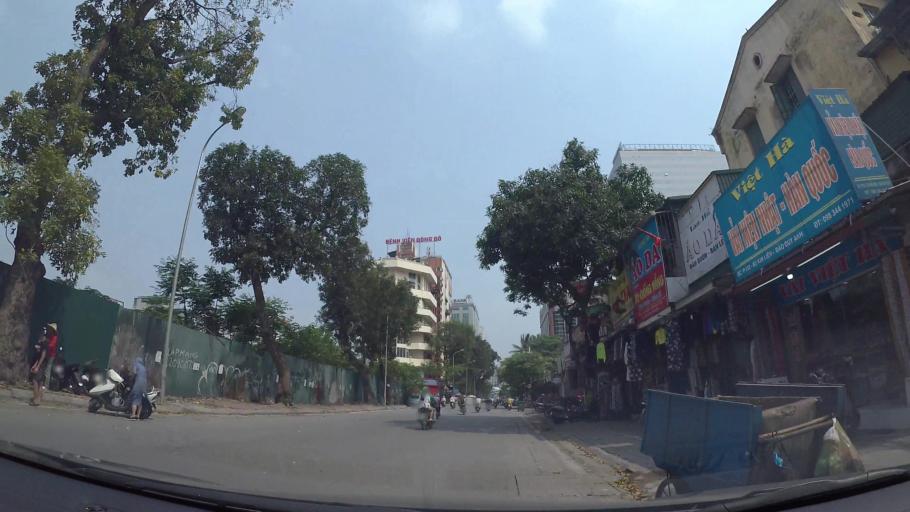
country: VN
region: Ha Noi
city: Hai BaTrung
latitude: 21.0099
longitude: 105.8372
